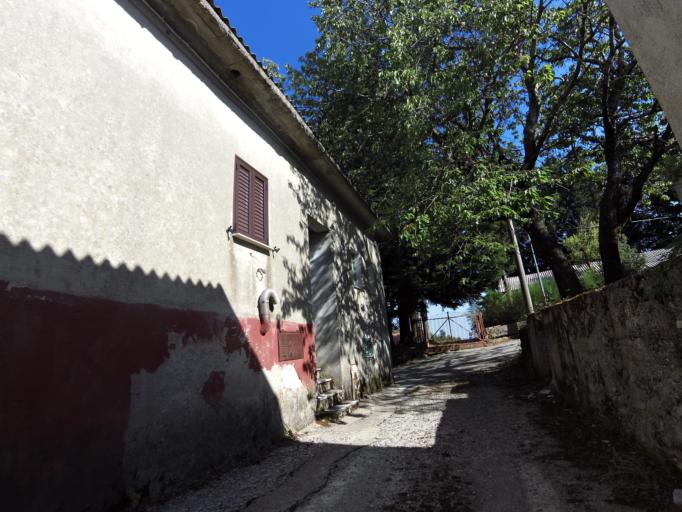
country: IT
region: Calabria
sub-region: Provincia di Vibo-Valentia
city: Nardodipace
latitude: 38.4748
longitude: 16.3966
